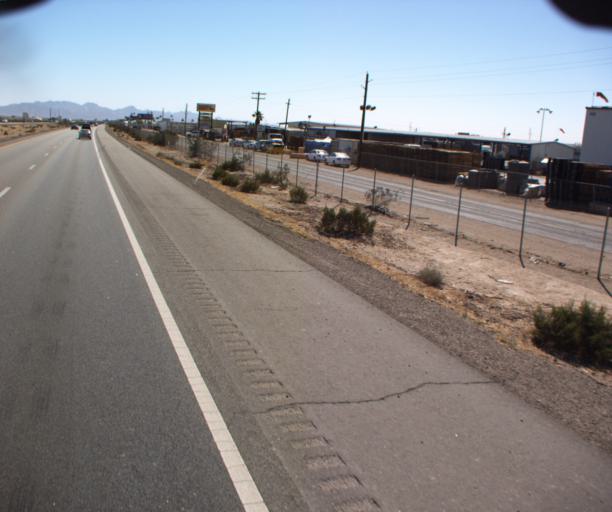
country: US
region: Arizona
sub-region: Yuma County
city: Yuma
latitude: 32.6844
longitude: -114.5632
